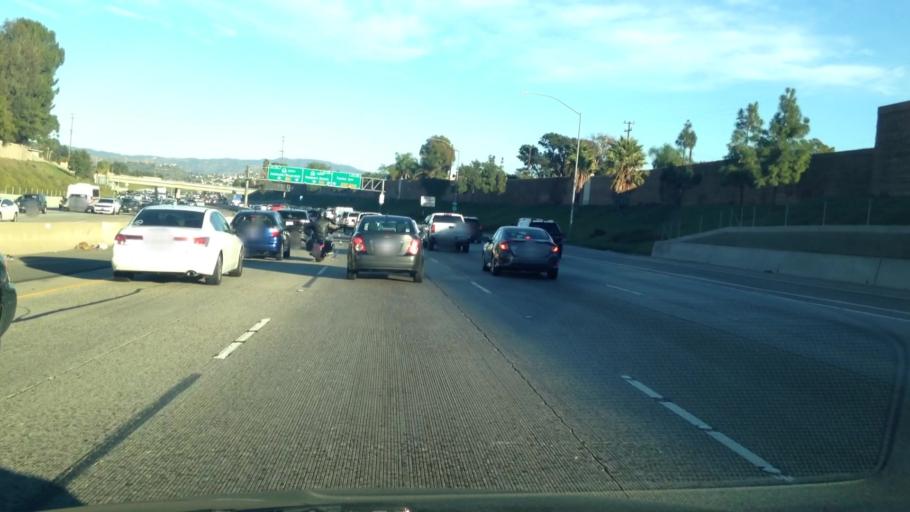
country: US
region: California
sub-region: Orange County
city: Orange
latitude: 33.7751
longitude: -117.8493
